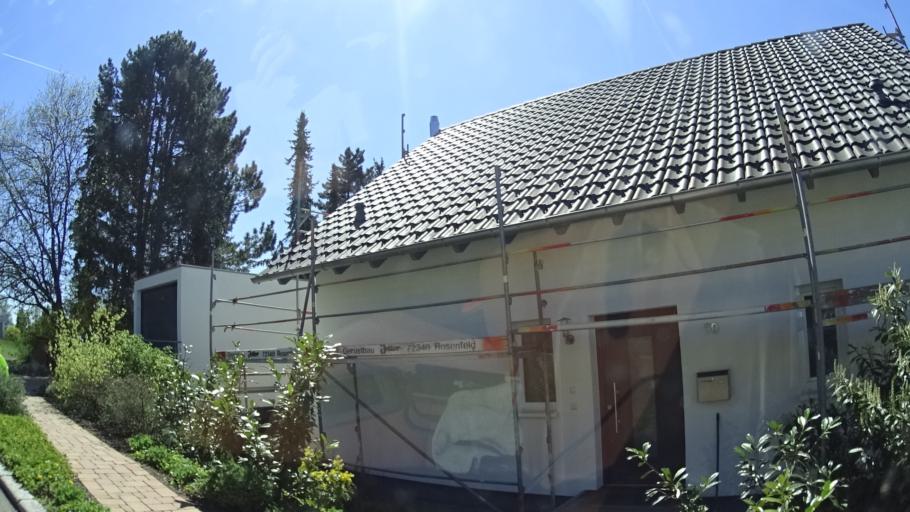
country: DE
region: Baden-Wuerttemberg
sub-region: Freiburg Region
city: Rottweil
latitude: 48.1567
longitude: 8.6194
